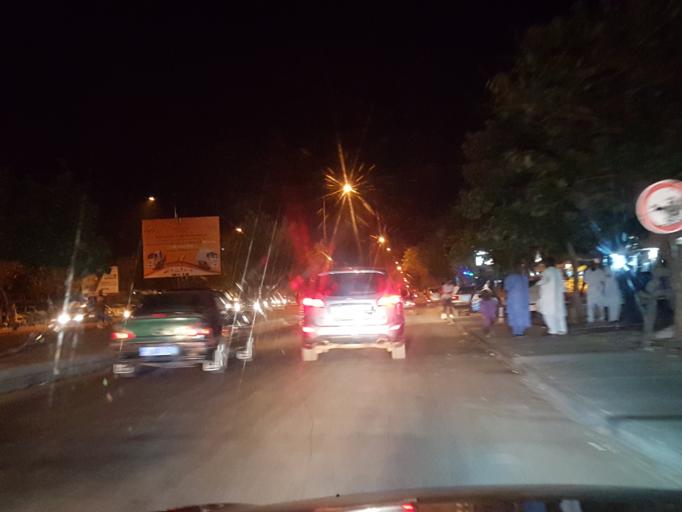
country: SN
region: Dakar
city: Grand Dakar
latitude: 14.7306
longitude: -17.4585
